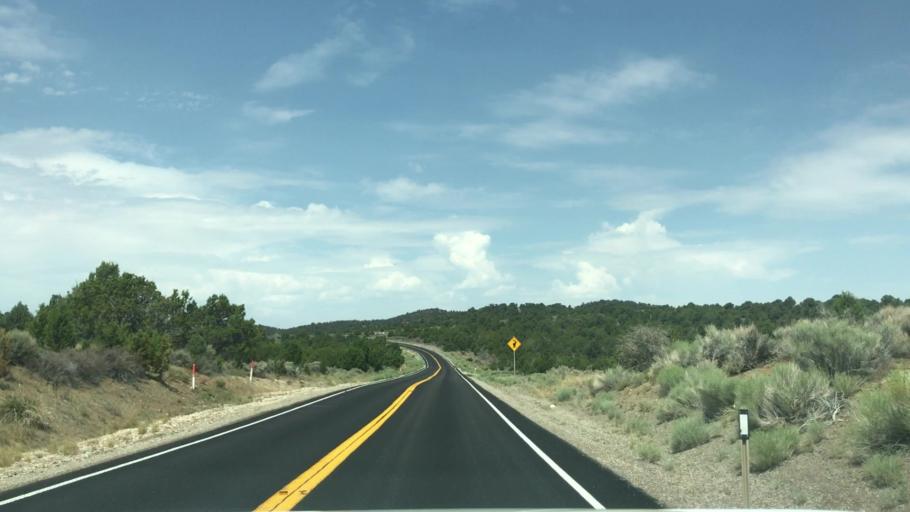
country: US
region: Nevada
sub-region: Eureka County
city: Eureka
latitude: 39.3945
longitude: -115.4608
